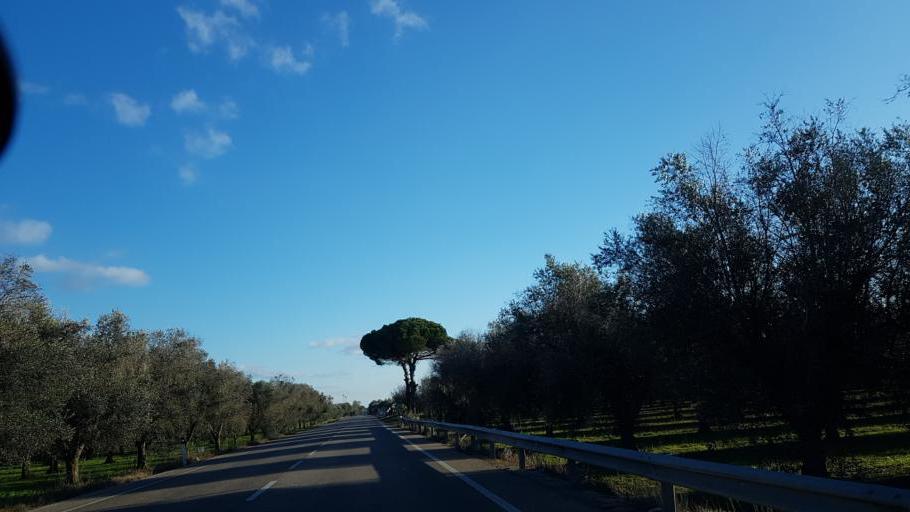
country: IT
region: Apulia
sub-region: Provincia di Lecce
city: Squinzano
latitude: 40.4524
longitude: 18.0270
